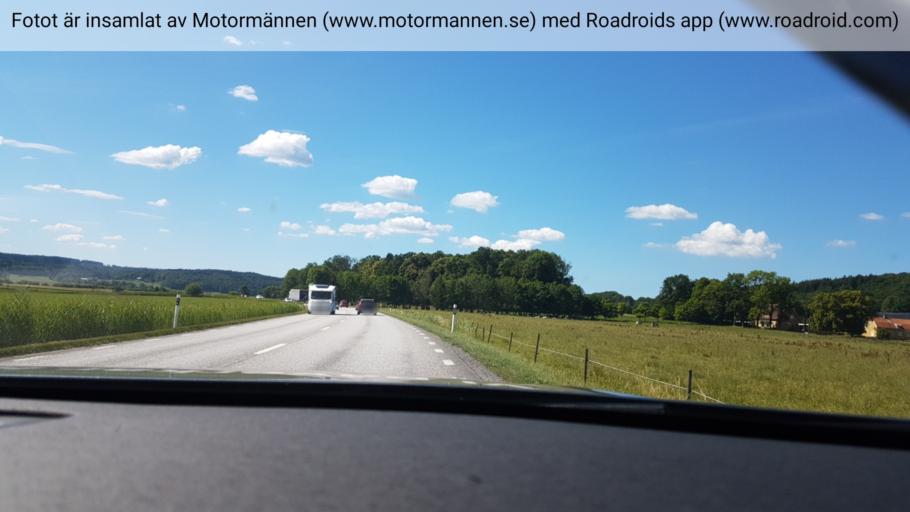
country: SE
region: Vaestra Goetaland
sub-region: Marks Kommun
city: Horred
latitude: 57.3346
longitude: 12.4475
